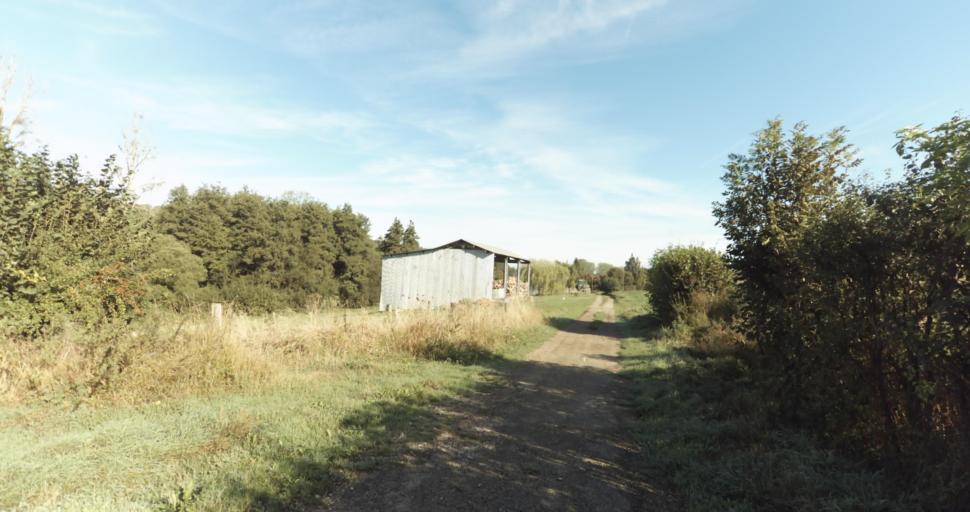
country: FR
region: Lower Normandy
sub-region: Departement de l'Orne
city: Vimoutiers
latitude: 48.9276
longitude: 0.2718
